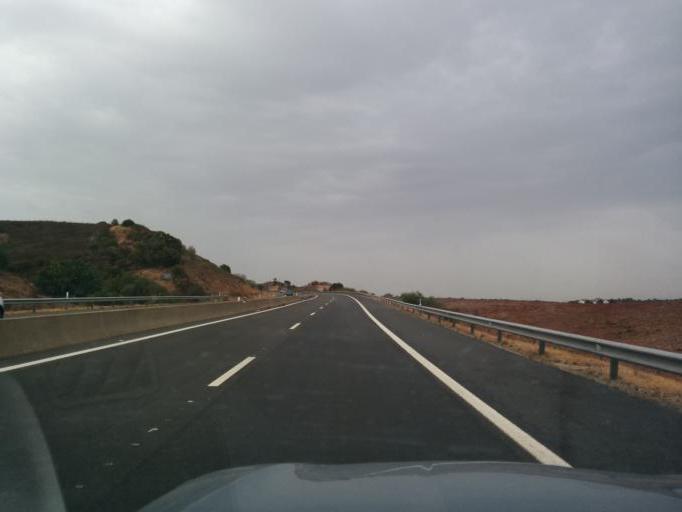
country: PT
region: Faro
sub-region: Tavira
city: Tavira
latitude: 37.1720
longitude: -7.6181
